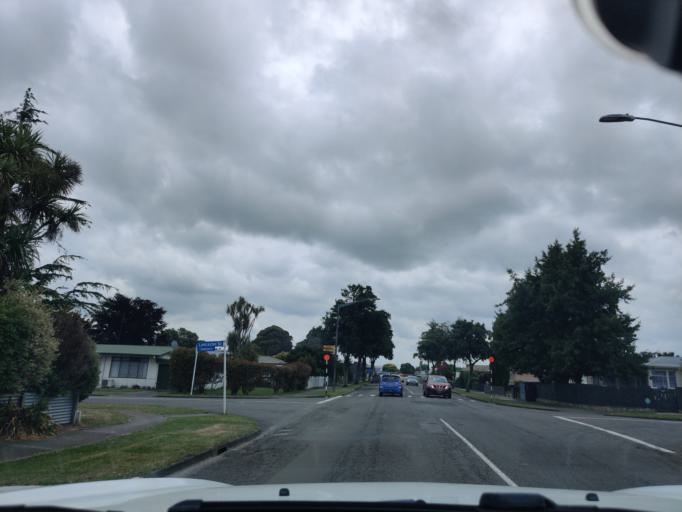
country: NZ
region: Manawatu-Wanganui
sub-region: Palmerston North City
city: Palmerston North
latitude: -40.3524
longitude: 175.5859
